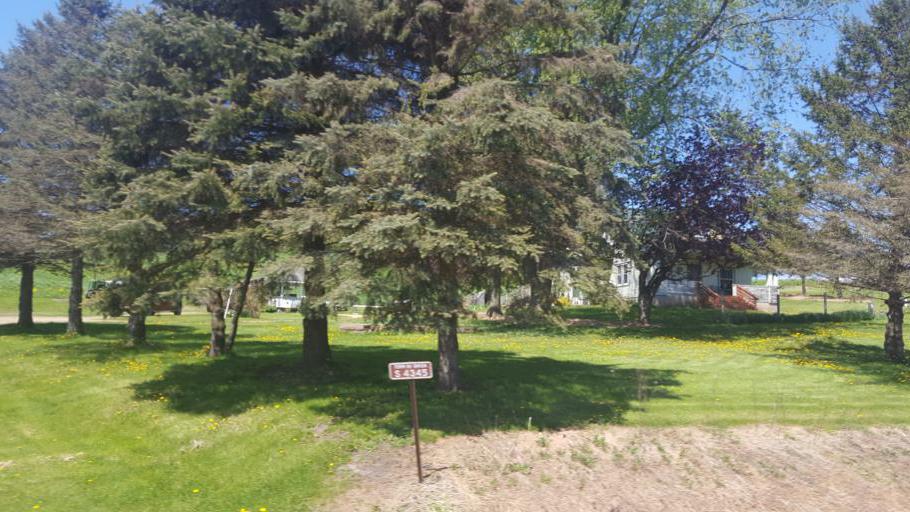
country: US
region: Wisconsin
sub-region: Vernon County
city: Hillsboro
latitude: 43.5736
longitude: -90.4423
